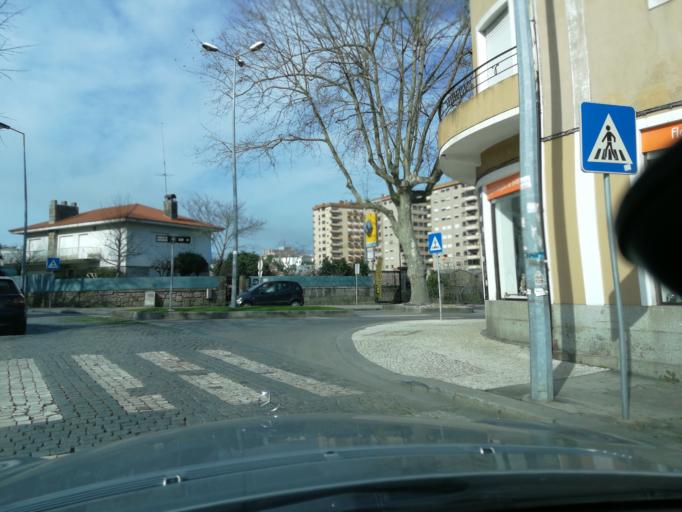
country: PT
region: Braga
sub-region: Vila Nova de Famalicao
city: Vila Nova de Famalicao
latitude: 41.4070
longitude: -8.5238
